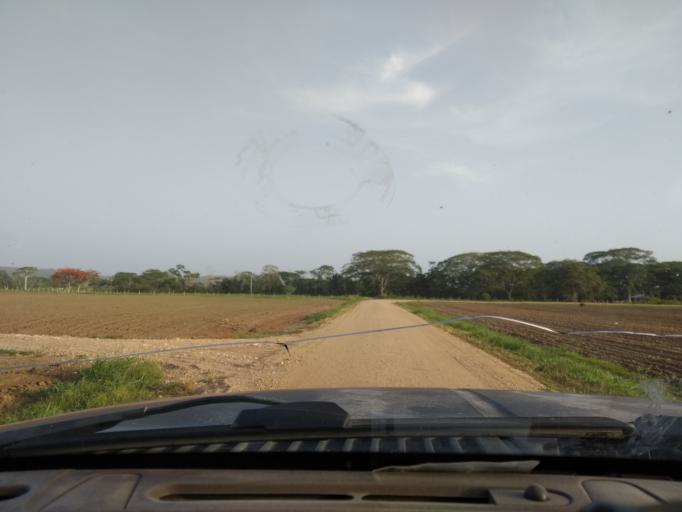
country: BZ
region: Cayo
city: San Ignacio
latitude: 17.2186
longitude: -88.9985
